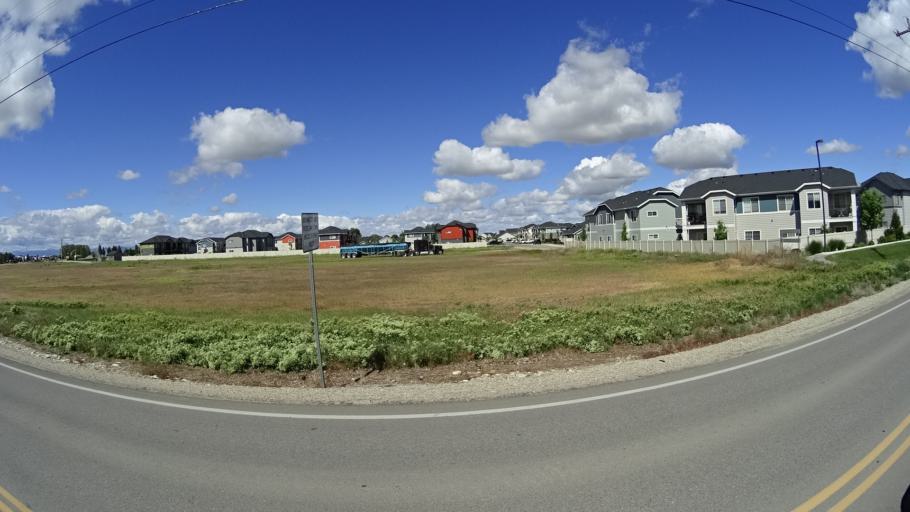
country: US
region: Idaho
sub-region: Ada County
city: Kuna
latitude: 43.5042
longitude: -116.4338
